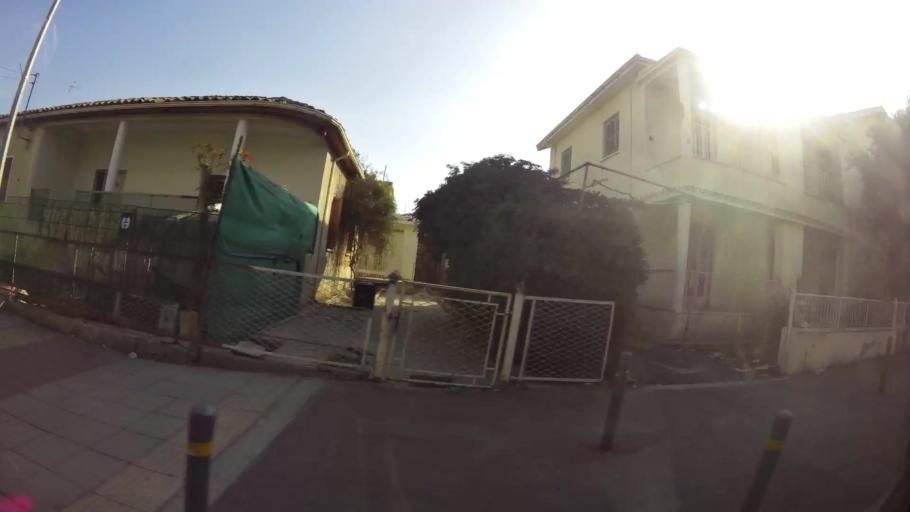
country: CY
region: Lefkosia
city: Nicosia
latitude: 35.1773
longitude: 33.3367
